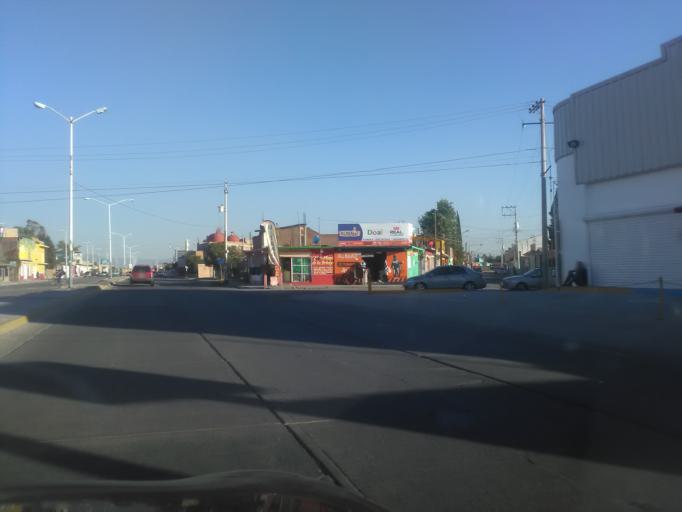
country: MX
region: Durango
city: Victoria de Durango
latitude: 24.0591
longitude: -104.5924
